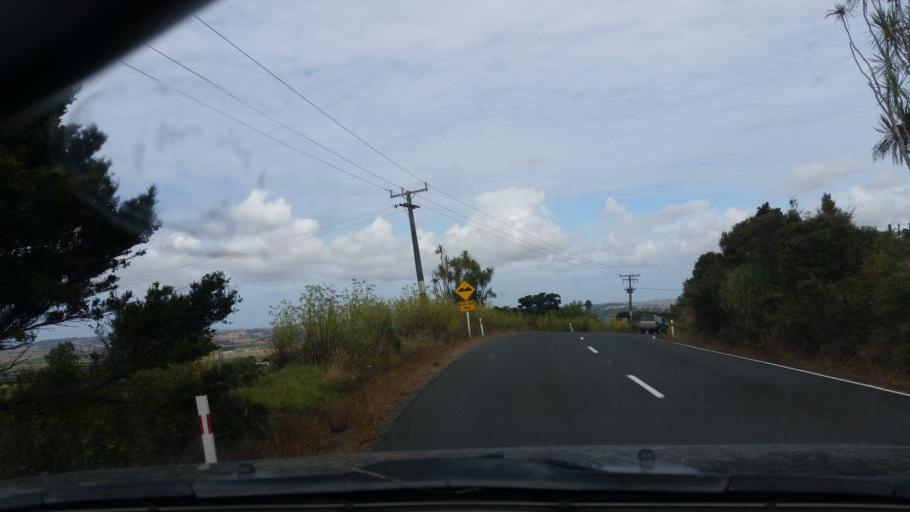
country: NZ
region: Northland
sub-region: Kaipara District
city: Dargaville
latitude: -35.9485
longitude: 173.9121
